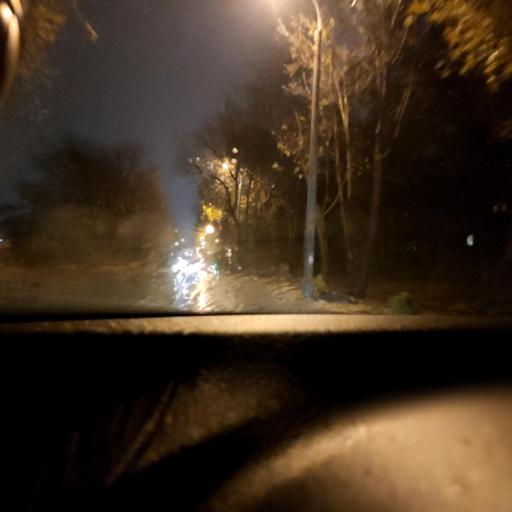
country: RU
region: Samara
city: Samara
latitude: 53.2248
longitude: 50.2102
